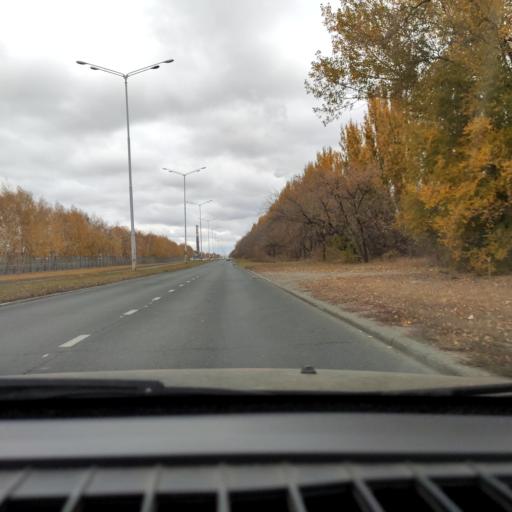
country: RU
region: Samara
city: Tol'yatti
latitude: 53.5680
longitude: 49.2761
